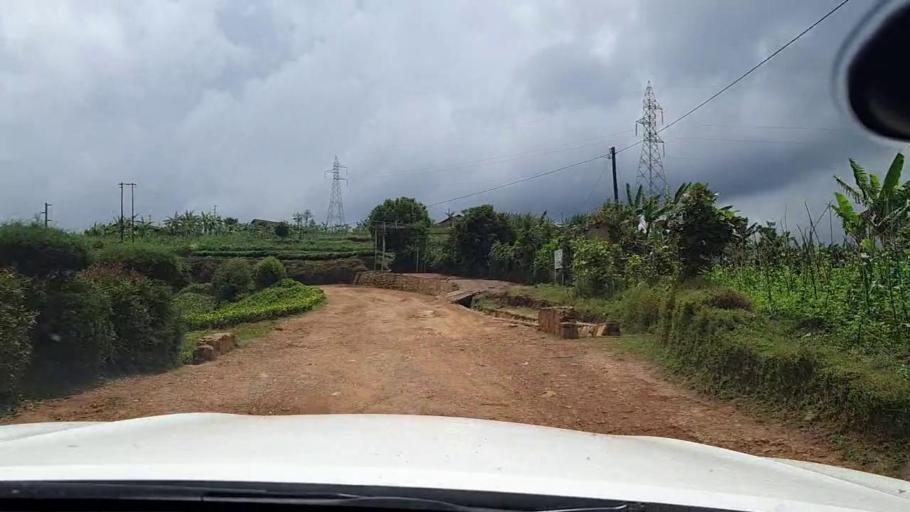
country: RW
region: Western Province
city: Kibuye
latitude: -2.1708
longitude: 29.4325
